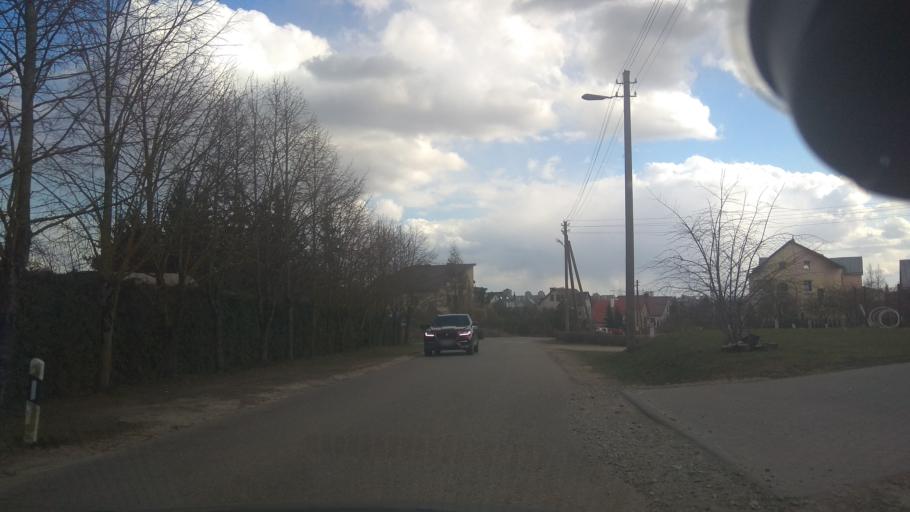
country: LT
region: Vilnius County
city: Pasilaiciai
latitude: 54.7408
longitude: 25.2018
